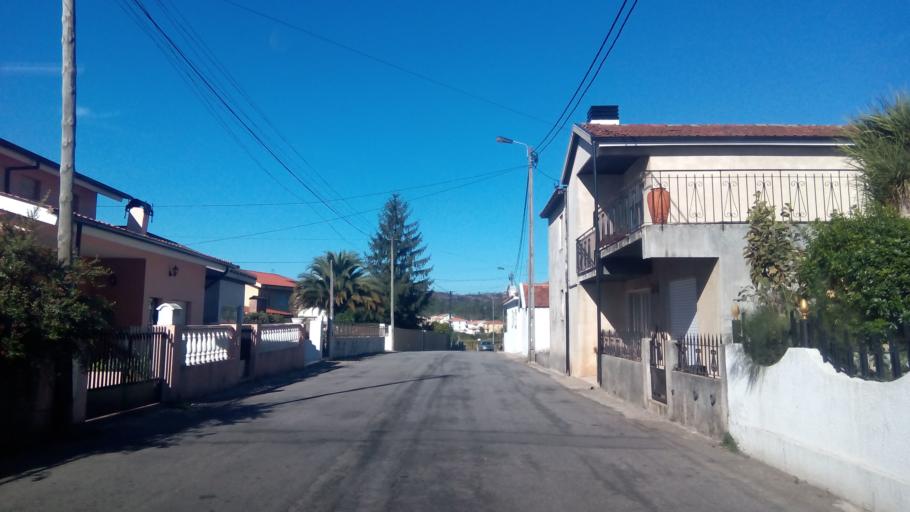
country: PT
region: Porto
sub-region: Paredes
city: Gandra
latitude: 41.1914
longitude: -8.4474
